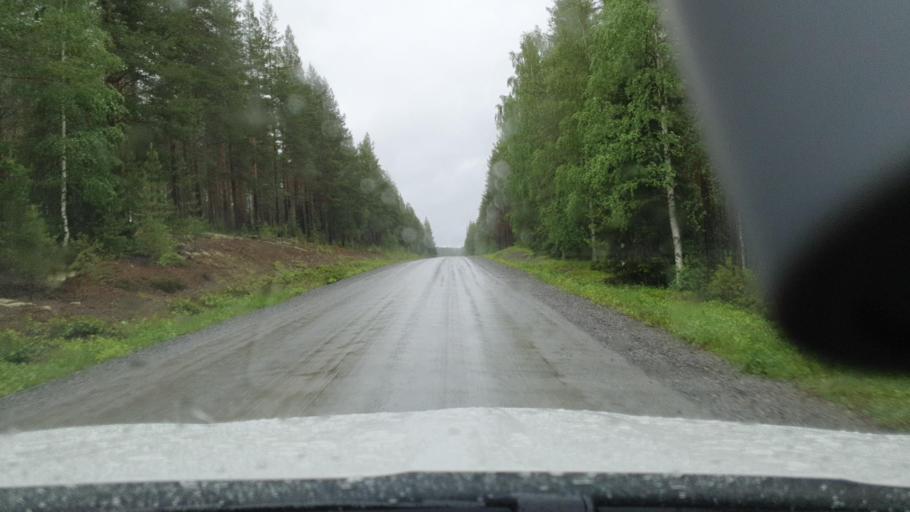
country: SE
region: Vaesterbotten
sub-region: Skelleftea Kommun
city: Burtraesk
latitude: 64.3814
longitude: 20.3311
